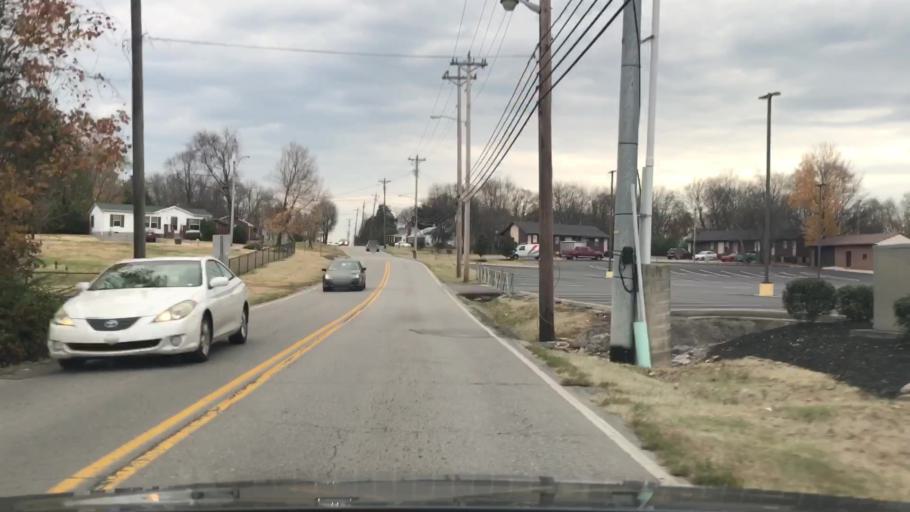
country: US
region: Tennessee
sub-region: Wilson County
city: Lebanon
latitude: 36.2161
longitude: -86.2832
